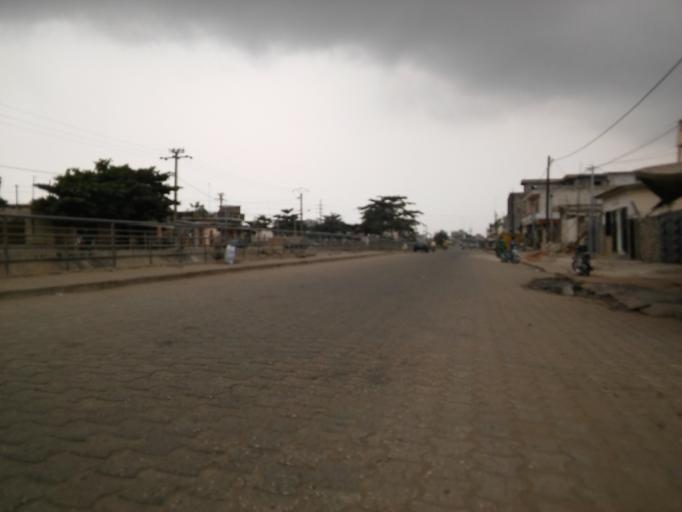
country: BJ
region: Littoral
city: Cotonou
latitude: 6.3782
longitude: 2.3974
